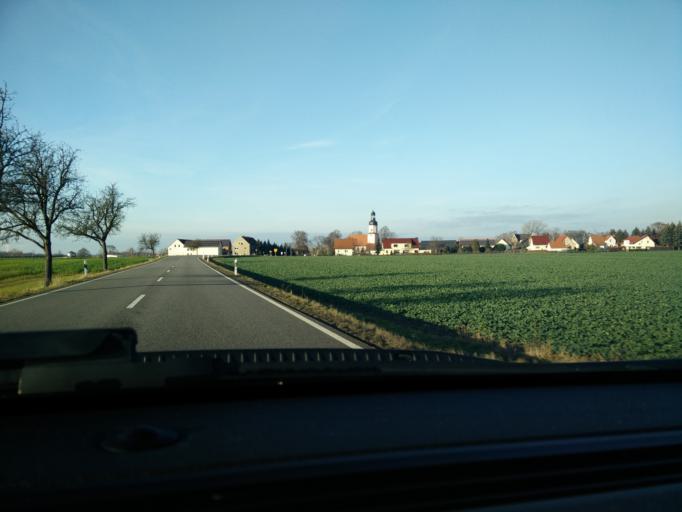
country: DE
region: Saxony
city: Geithain
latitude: 51.0968
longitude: 12.6995
